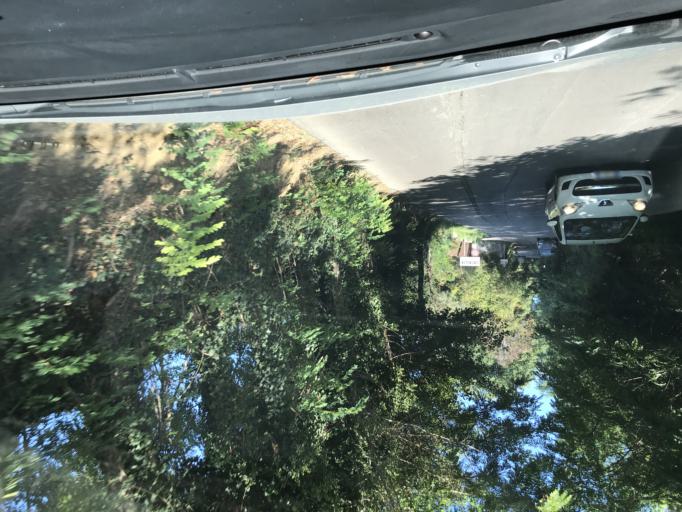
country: IT
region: Umbria
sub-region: Provincia di Perugia
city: Ponte Felcino
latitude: 43.1062
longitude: 12.4383
